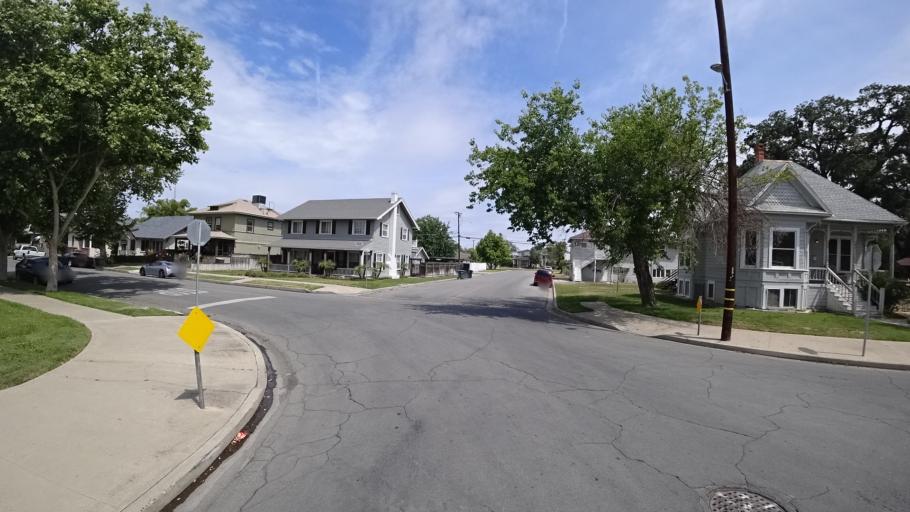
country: US
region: California
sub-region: Kings County
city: Hanford
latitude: 36.3312
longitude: -119.6507
